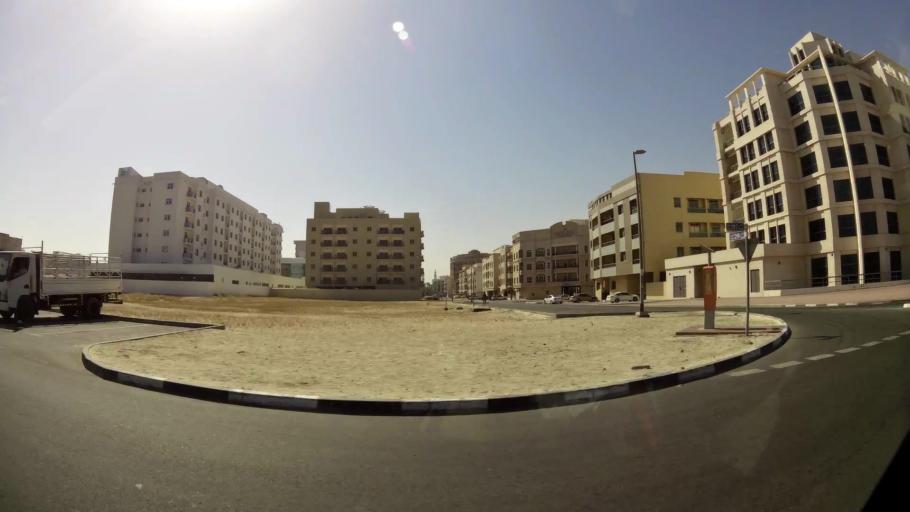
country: AE
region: Ash Shariqah
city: Sharjah
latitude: 25.2531
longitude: 55.2843
